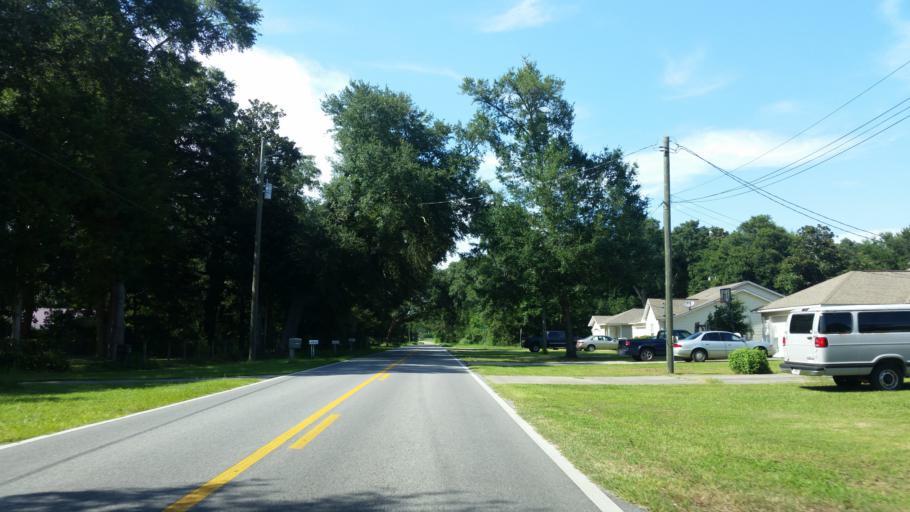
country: US
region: Florida
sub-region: Santa Rosa County
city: Pace
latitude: 30.5830
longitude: -87.1614
